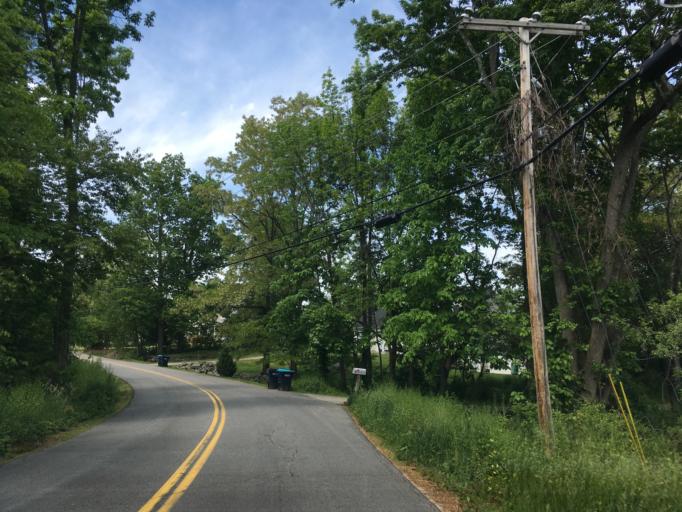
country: US
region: New Hampshire
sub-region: Rockingham County
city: Stratham Station
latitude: 43.0288
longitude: -70.8705
